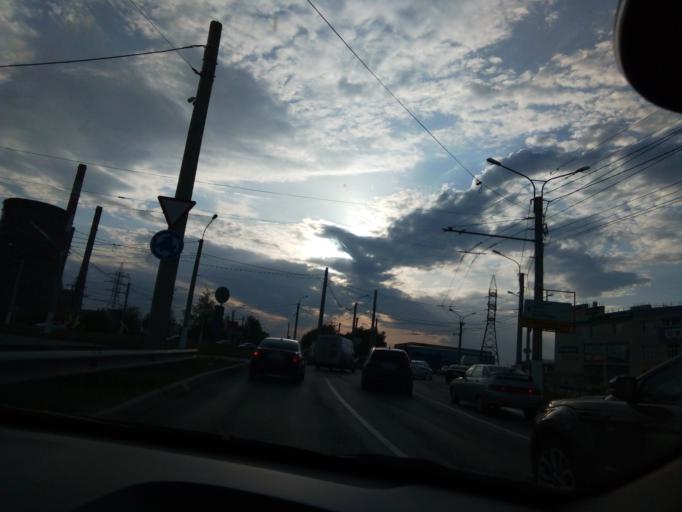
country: RU
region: Chuvashia
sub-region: Cheboksarskiy Rayon
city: Cheboksary
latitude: 56.1281
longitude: 47.3116
